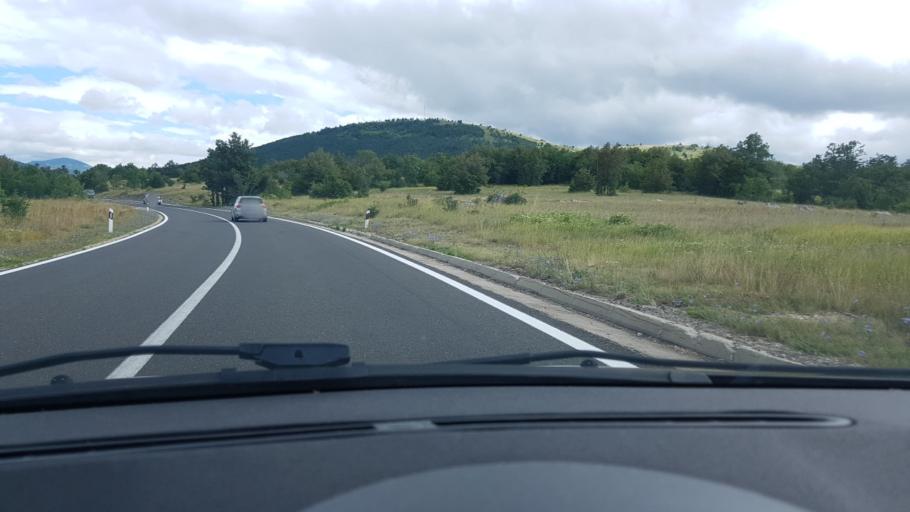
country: HR
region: Zadarska
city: Gracac
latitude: 44.4230
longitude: 15.8761
